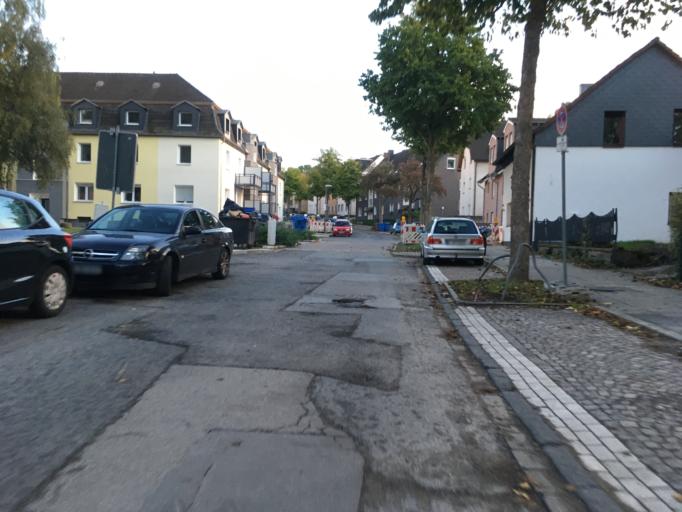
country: DE
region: North Rhine-Westphalia
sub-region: Regierungsbezirk Munster
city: Bottrop
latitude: 51.4861
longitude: 6.9255
